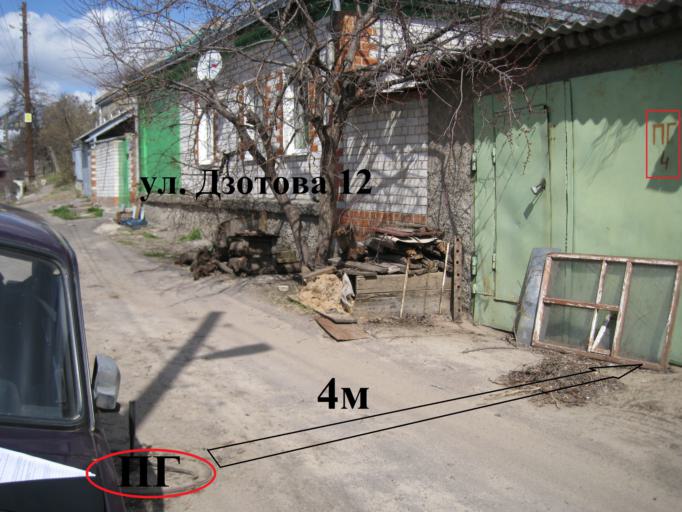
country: RU
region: Voronezj
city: Voronezh
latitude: 51.6311
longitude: 39.1966
